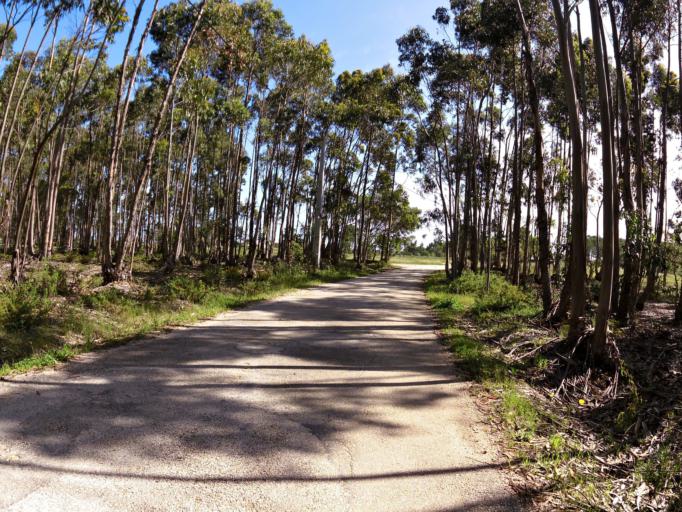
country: PT
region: Faro
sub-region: Aljezur
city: Aljezur
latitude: 37.3387
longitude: -8.8075
